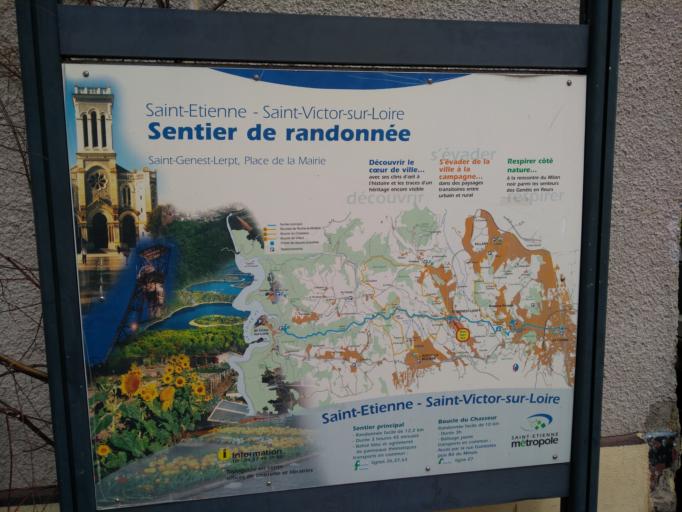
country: FR
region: Rhone-Alpes
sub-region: Departement de la Loire
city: Saint-Genest-Lerpt
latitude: 45.4465
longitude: 4.3360
